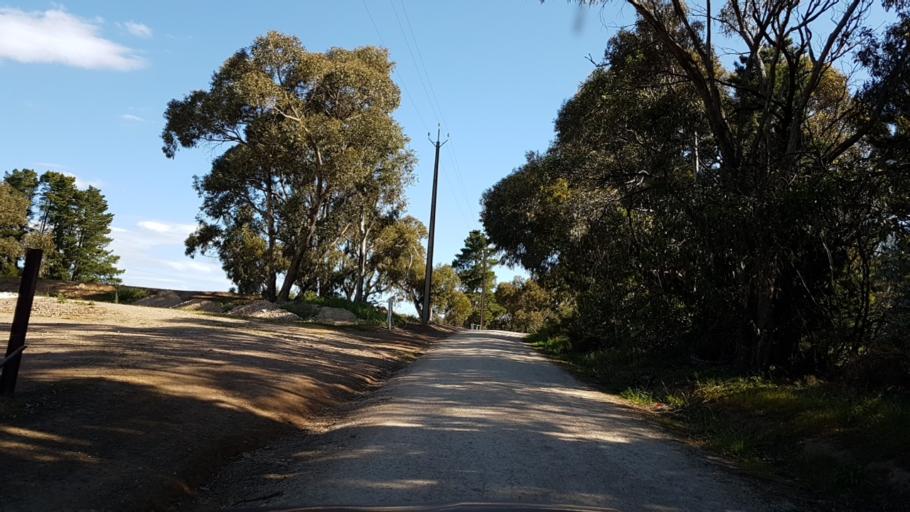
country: AU
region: South Australia
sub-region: Tea Tree Gully
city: Hope Valley
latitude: -34.8486
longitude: 138.7669
